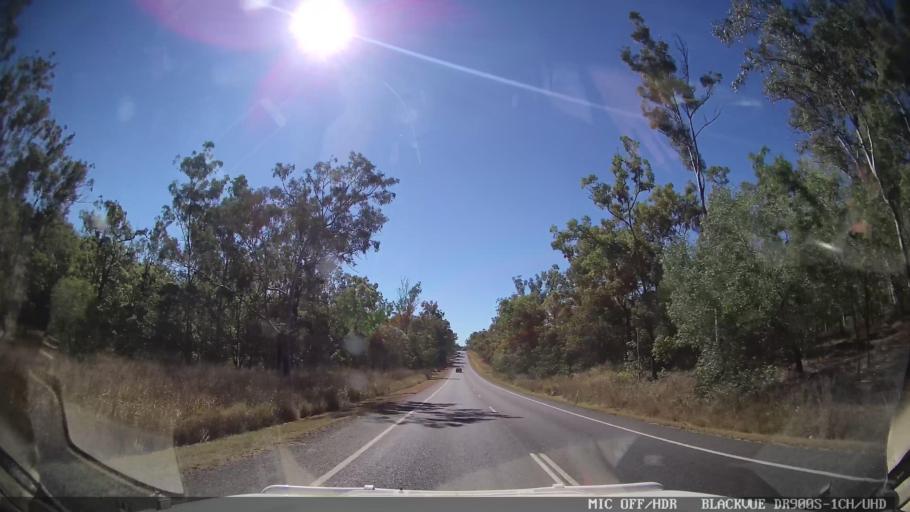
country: AU
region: Queensland
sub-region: Gladstone
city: Toolooa
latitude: -23.9704
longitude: 151.2174
